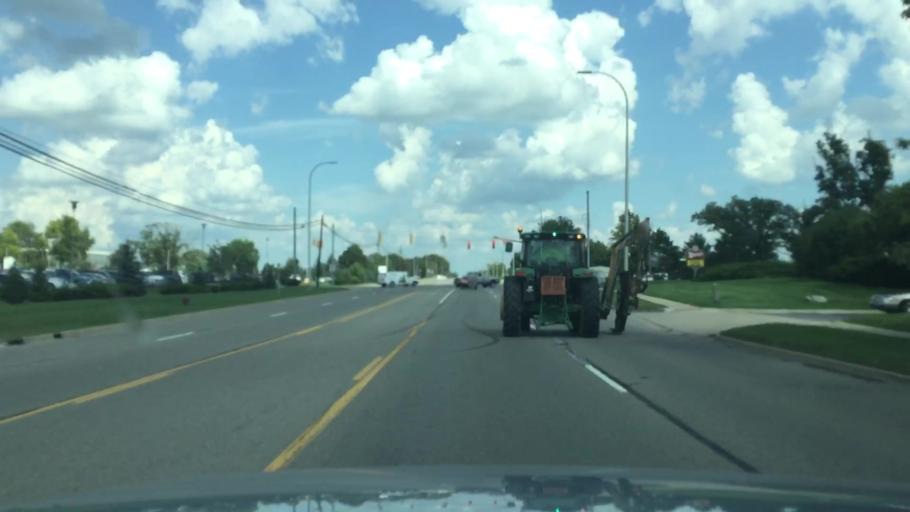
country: US
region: Michigan
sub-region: Washtenaw County
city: Saline
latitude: 42.1728
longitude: -83.7675
